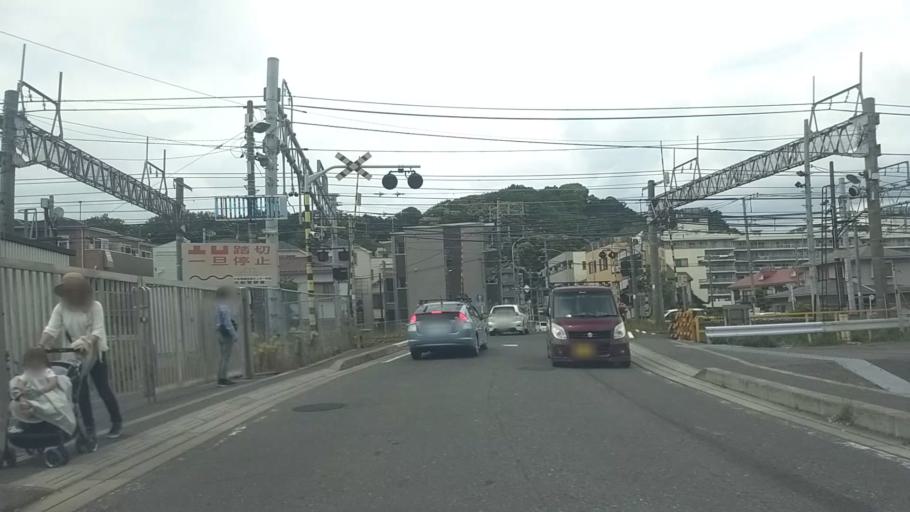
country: JP
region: Kanagawa
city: Kamakura
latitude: 35.3492
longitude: 139.5286
